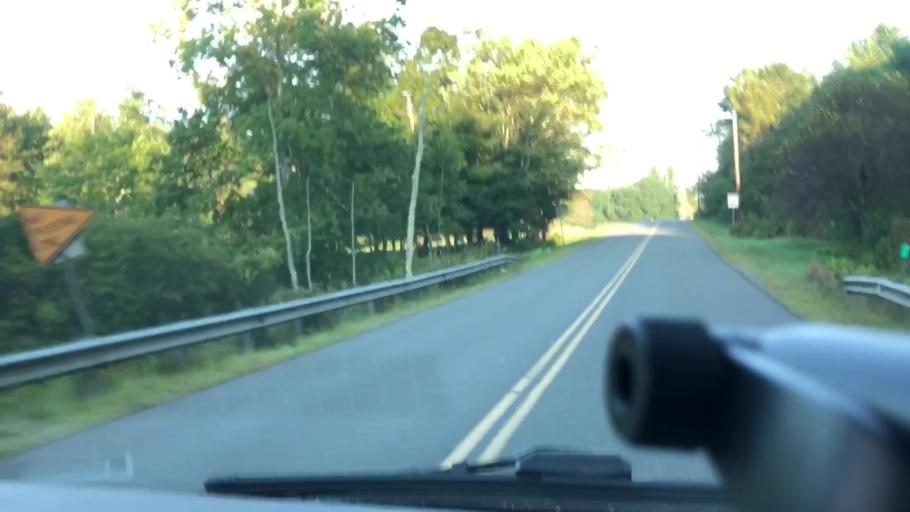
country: US
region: Massachusetts
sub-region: Franklin County
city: Ashfield
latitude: 42.4961
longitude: -72.8665
